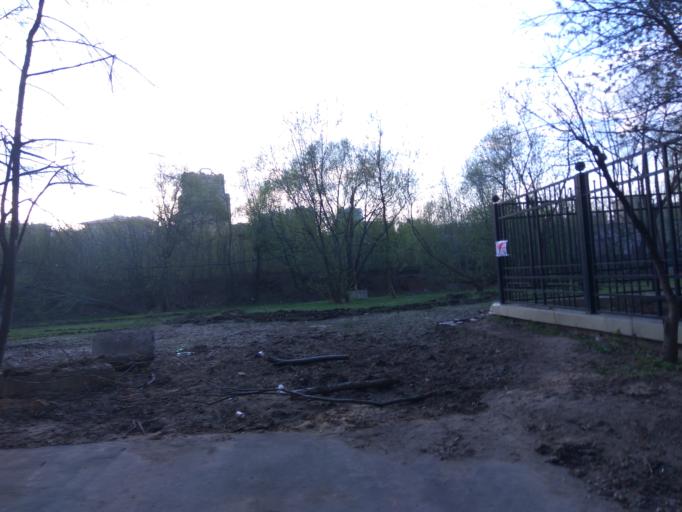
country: RU
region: Moskovskaya
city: Semenovskoye
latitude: 55.6874
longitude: 37.5616
